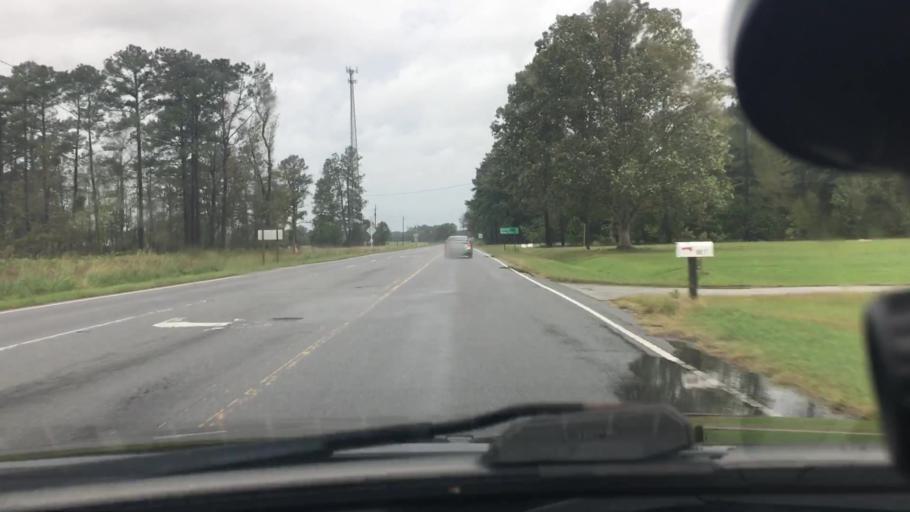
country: US
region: North Carolina
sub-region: Craven County
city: Vanceboro
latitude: 35.4187
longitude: -77.2567
